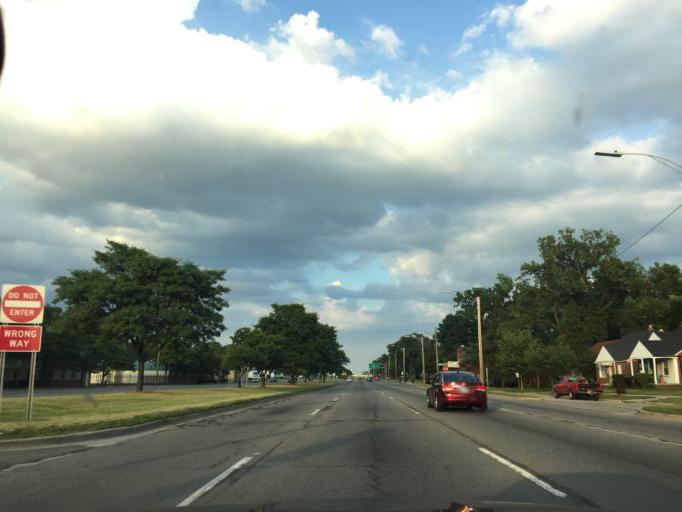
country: US
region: Michigan
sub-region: Oakland County
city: Ferndale
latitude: 42.4462
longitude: -83.1368
